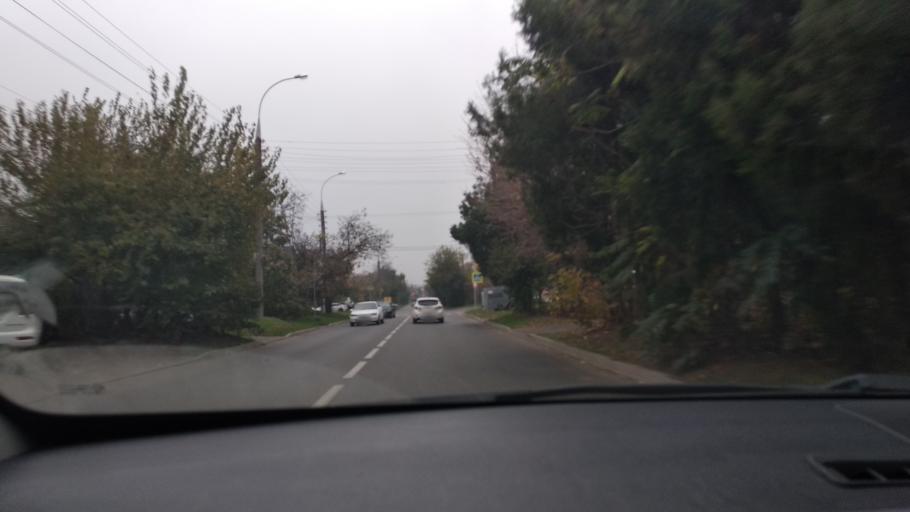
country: RU
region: Krasnodarskiy
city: Krasnodar
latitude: 45.0186
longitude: 39.0103
